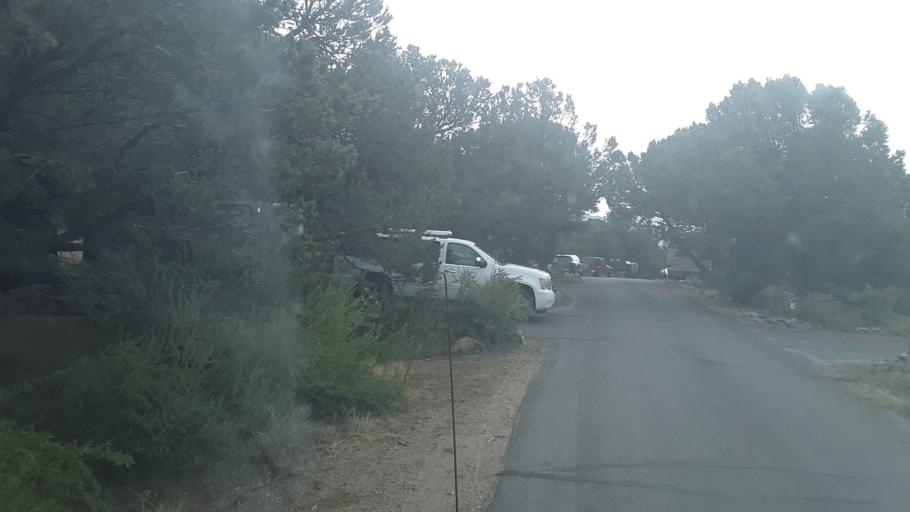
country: US
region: Colorado
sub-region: Custer County
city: Westcliffe
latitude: 37.7477
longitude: -105.5043
